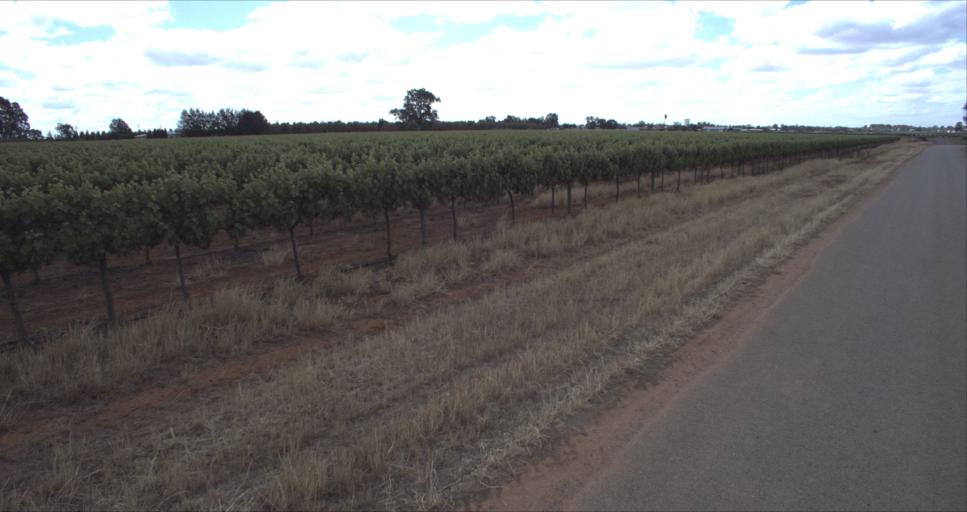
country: AU
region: New South Wales
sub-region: Leeton
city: Leeton
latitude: -34.5782
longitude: 146.4005
